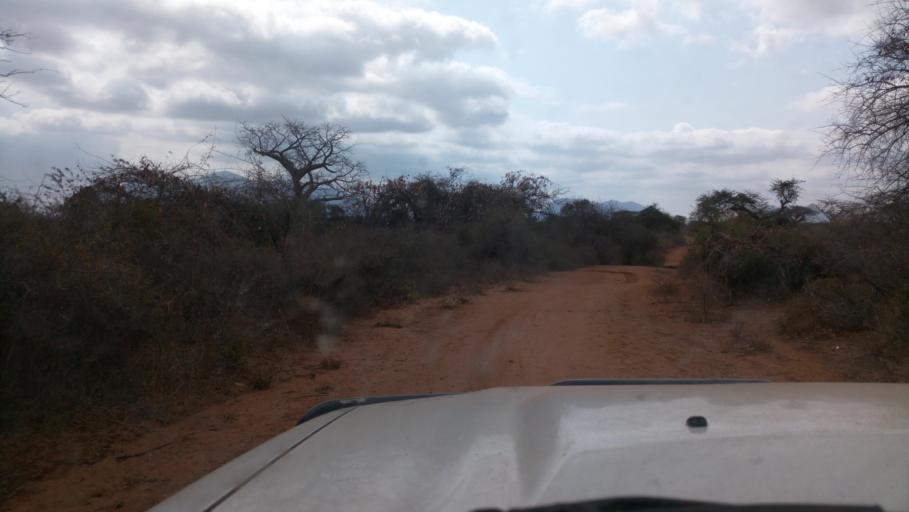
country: KE
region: Kitui
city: Kitui
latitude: -1.8318
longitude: 38.3152
